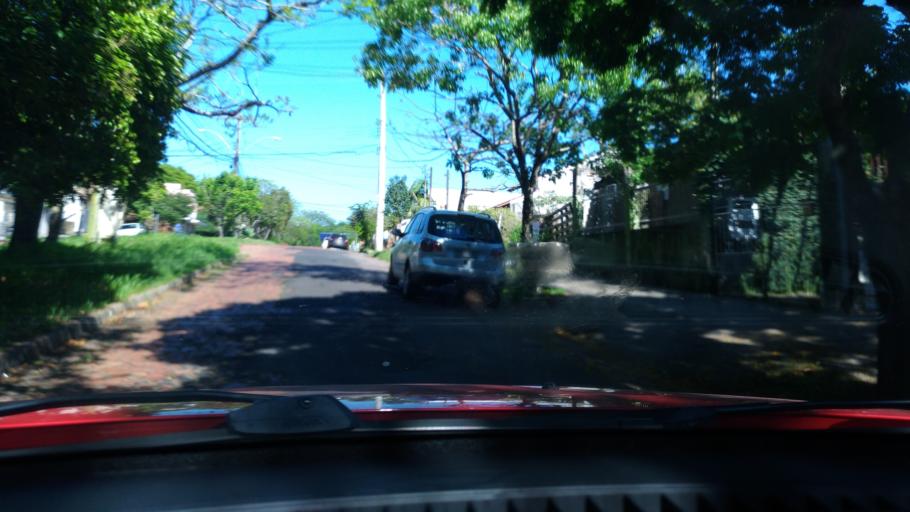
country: BR
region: Rio Grande do Sul
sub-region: Cachoeirinha
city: Cachoeirinha
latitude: -30.0334
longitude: -51.1336
